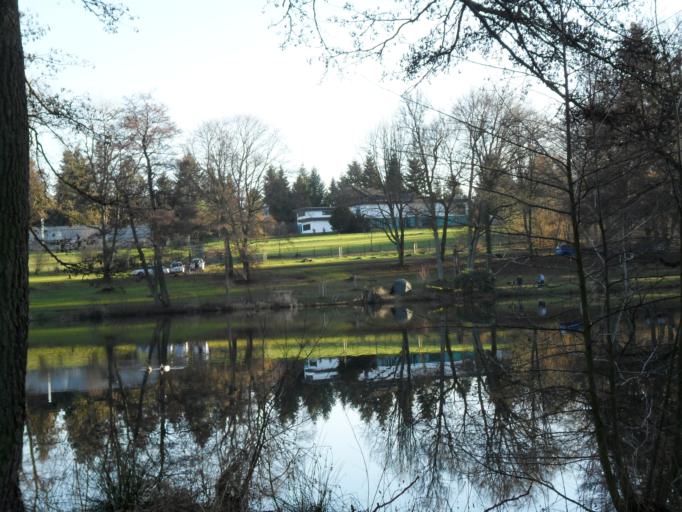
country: DE
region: Saarland
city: Kirkel
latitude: 49.3212
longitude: 7.2174
